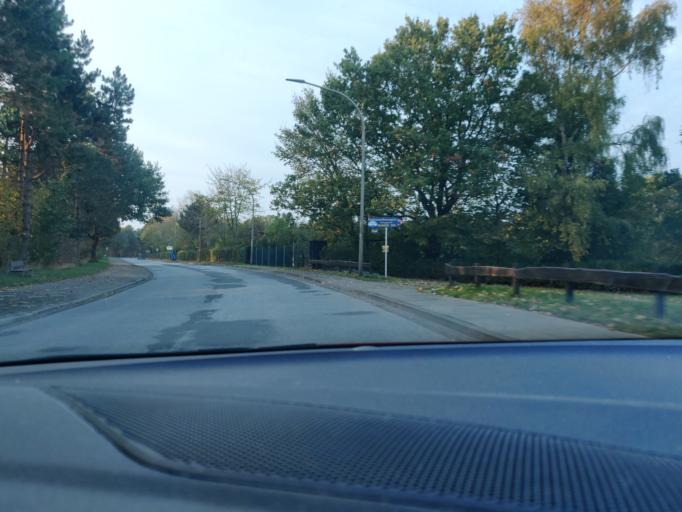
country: DE
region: Lower Saxony
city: Cuxhaven
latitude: 53.8768
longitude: 8.6522
